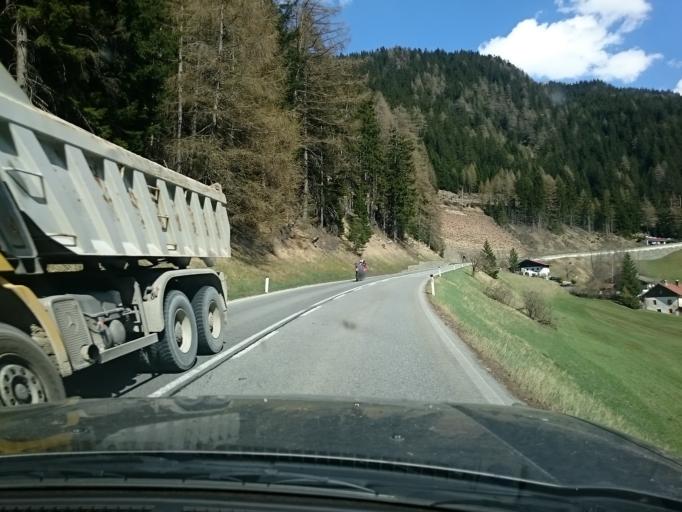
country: AT
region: Tyrol
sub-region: Politischer Bezirk Innsbruck Land
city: Gries am Brenner
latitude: 47.0273
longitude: 11.4982
